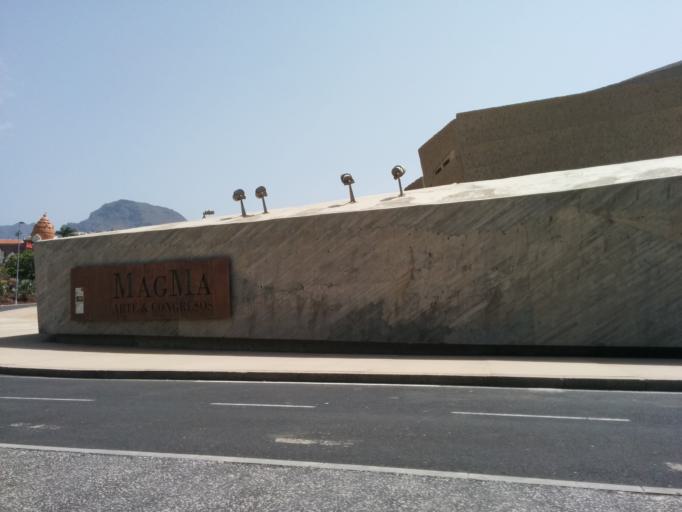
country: ES
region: Canary Islands
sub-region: Provincia de Santa Cruz de Tenerife
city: Playa de las Americas
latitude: 28.0698
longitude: -16.7277
